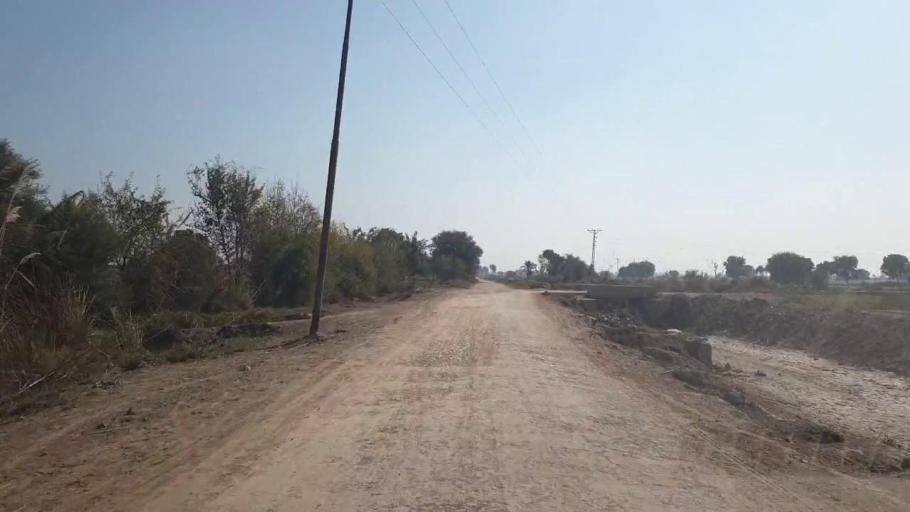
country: PK
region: Sindh
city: Shahdadpur
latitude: 25.9494
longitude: 68.6321
